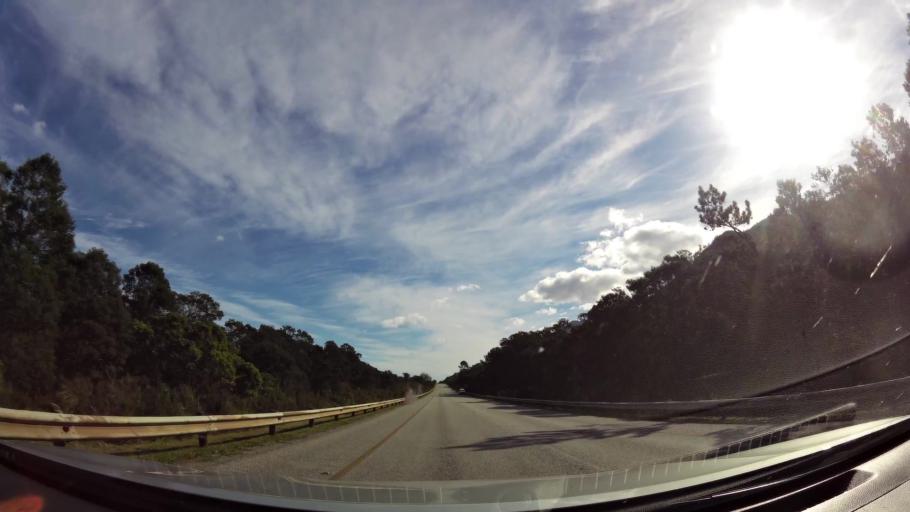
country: ZA
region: Eastern Cape
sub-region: Cacadu District Municipality
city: Kareedouw
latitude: -33.9923
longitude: 24.1628
